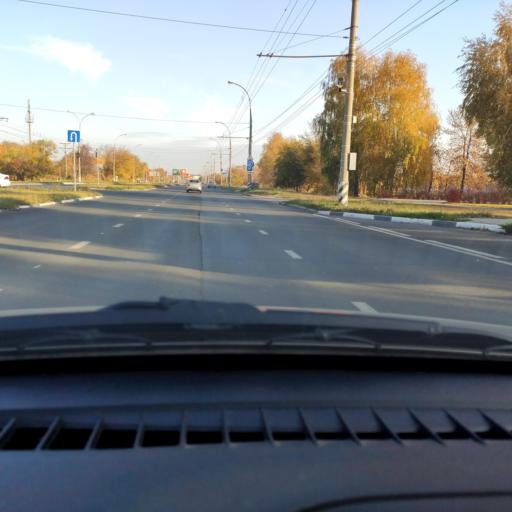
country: RU
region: Samara
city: Tol'yatti
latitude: 53.5430
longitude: 49.3009
